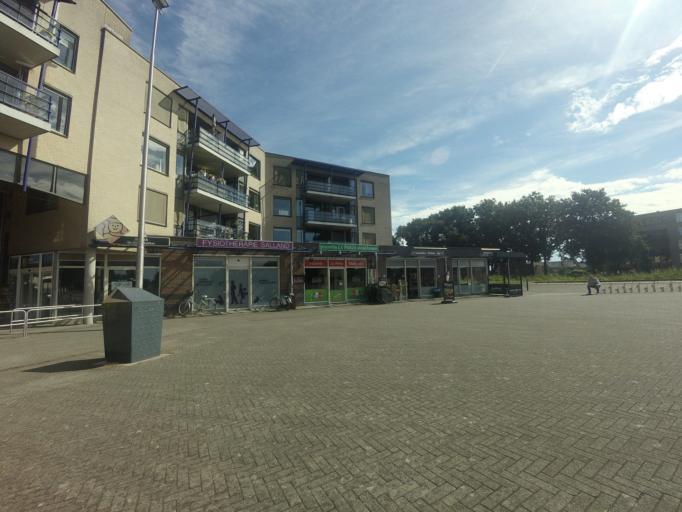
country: NL
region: Overijssel
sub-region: Gemeente Raalte
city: Raalte
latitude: 52.3928
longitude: 6.2868
